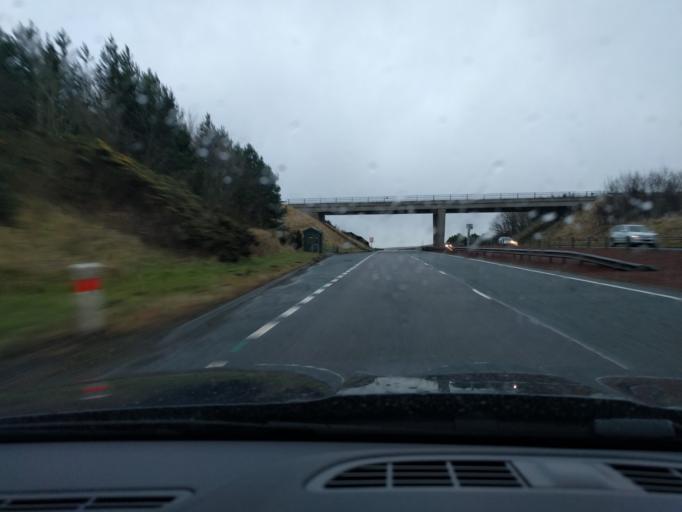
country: GB
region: England
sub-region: Northumberland
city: Berwick-Upon-Tweed
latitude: 55.8119
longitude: -2.0459
